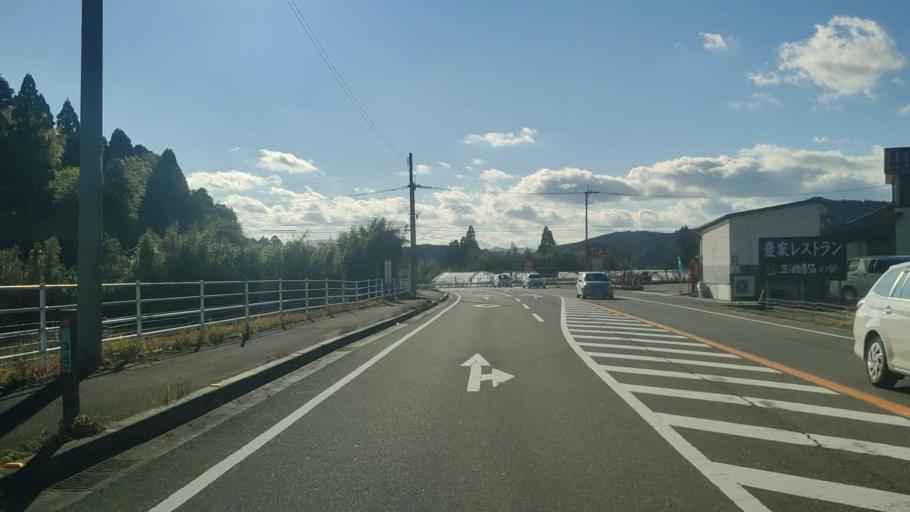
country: JP
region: Fukuoka
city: Maebaru-chuo
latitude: 33.4492
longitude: 130.2742
